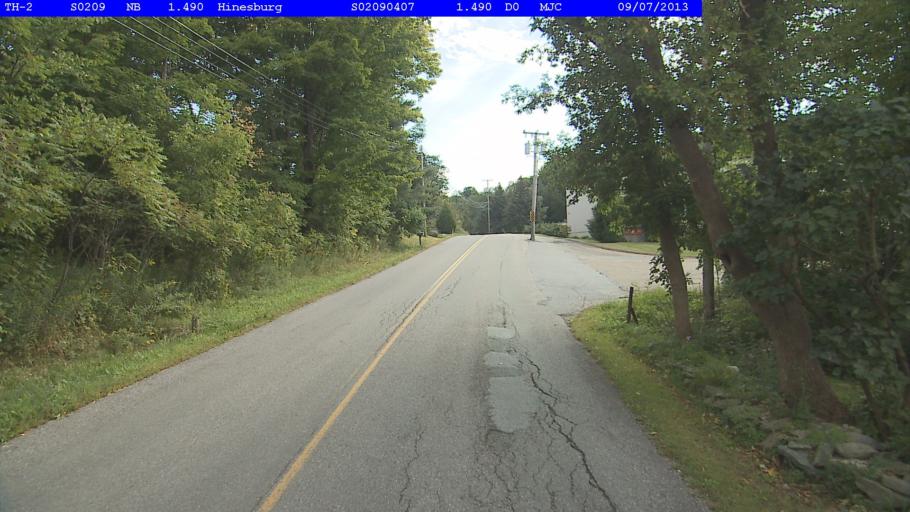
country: US
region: Vermont
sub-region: Chittenden County
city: Hinesburg
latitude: 44.3458
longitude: -73.0950
